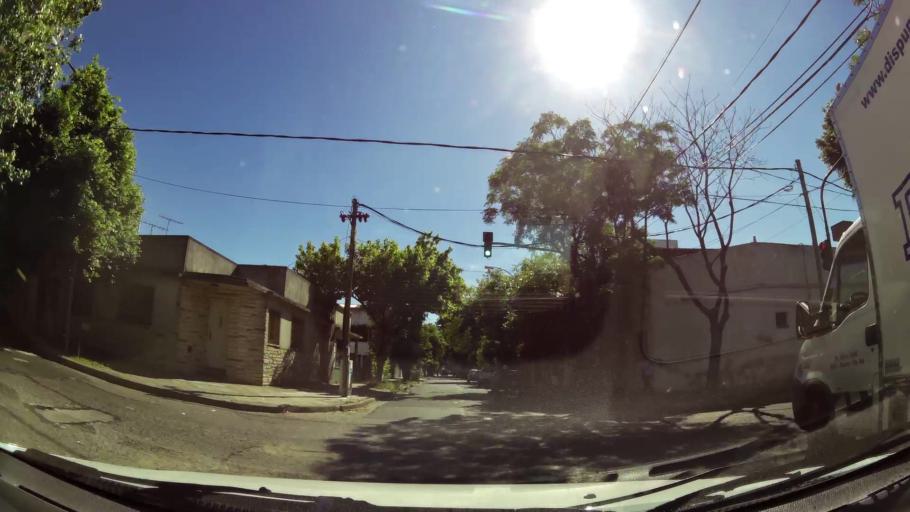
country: AR
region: Buenos Aires
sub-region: Partido de General San Martin
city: General San Martin
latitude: -34.5425
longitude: -58.5079
